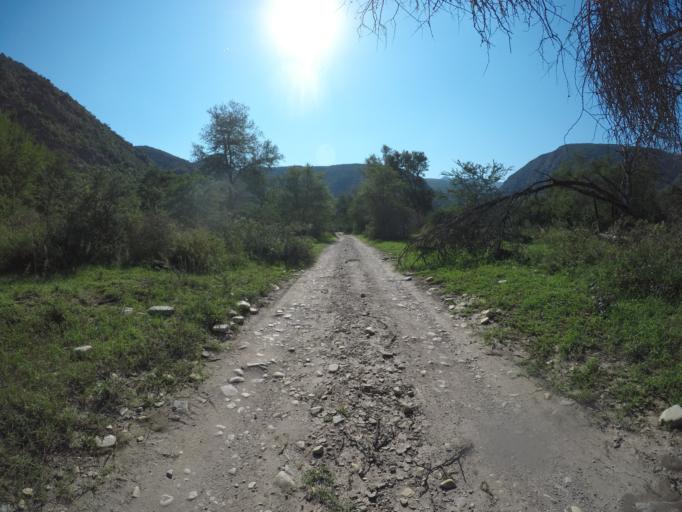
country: ZA
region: Eastern Cape
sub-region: Cacadu District Municipality
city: Kareedouw
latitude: -33.6573
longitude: 24.3660
